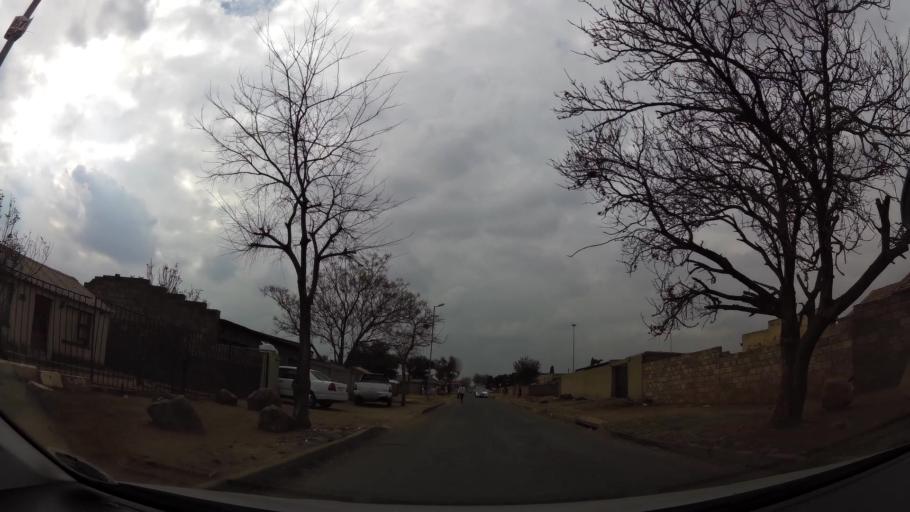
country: ZA
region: Gauteng
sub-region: City of Johannesburg Metropolitan Municipality
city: Soweto
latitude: -26.2639
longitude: 27.8511
